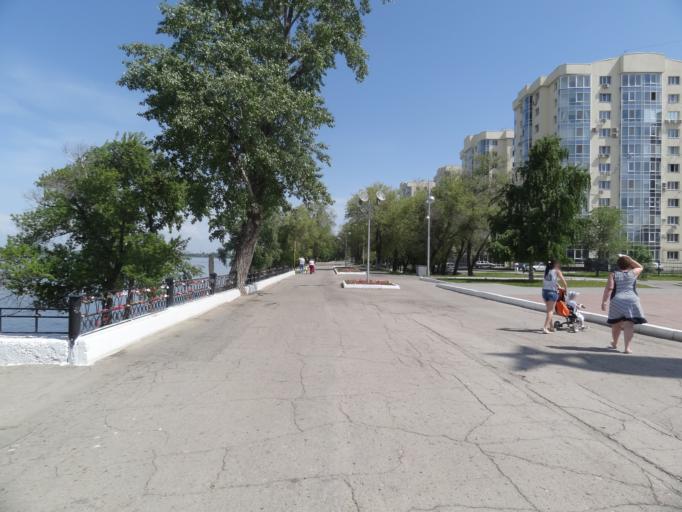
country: RU
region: Saratov
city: Engel's
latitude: 51.5037
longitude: 46.1261
